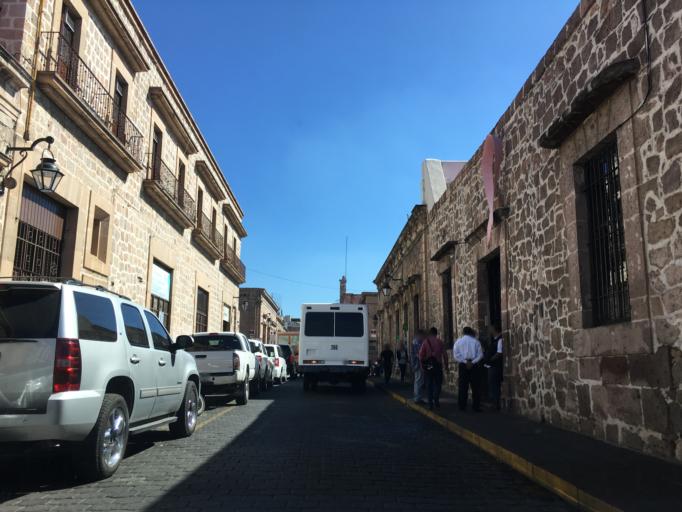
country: MX
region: Michoacan
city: Morelia
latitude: 19.7019
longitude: -101.1964
